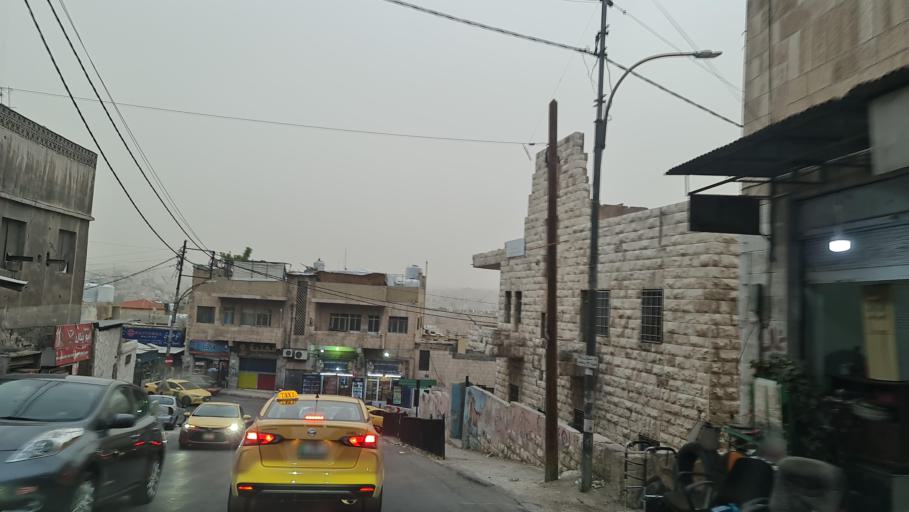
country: JO
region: Amman
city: Amman
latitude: 31.9479
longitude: 35.9415
